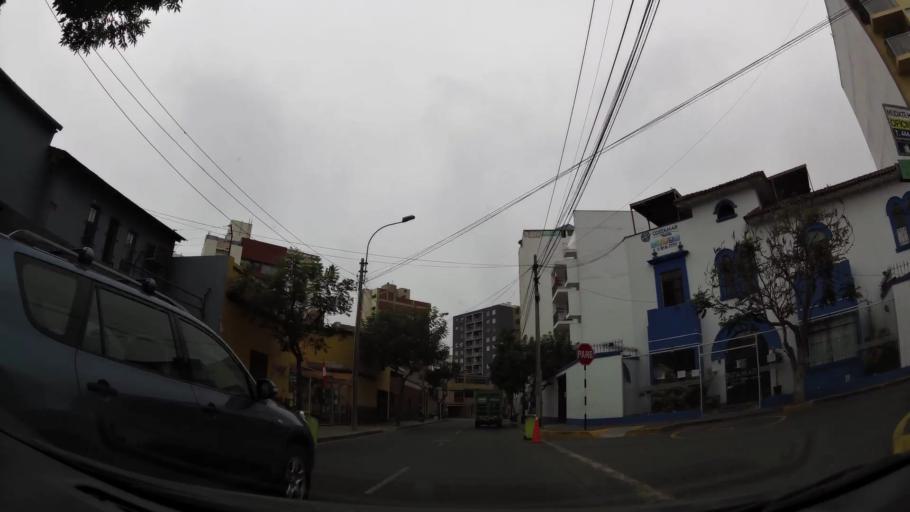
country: PE
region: Lima
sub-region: Lima
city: San Isidro
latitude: -12.1209
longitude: -77.0332
